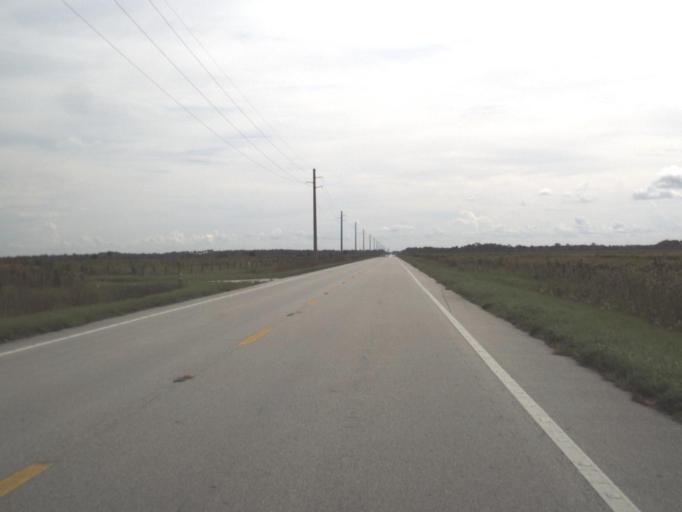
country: US
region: Florida
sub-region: Highlands County
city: Placid Lakes
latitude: 27.2090
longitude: -81.5274
